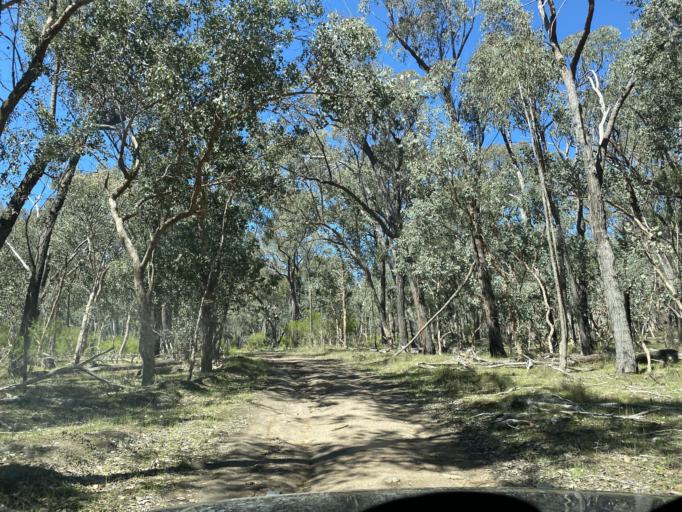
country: AU
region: Victoria
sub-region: Benalla
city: Benalla
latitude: -36.7032
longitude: 146.1524
